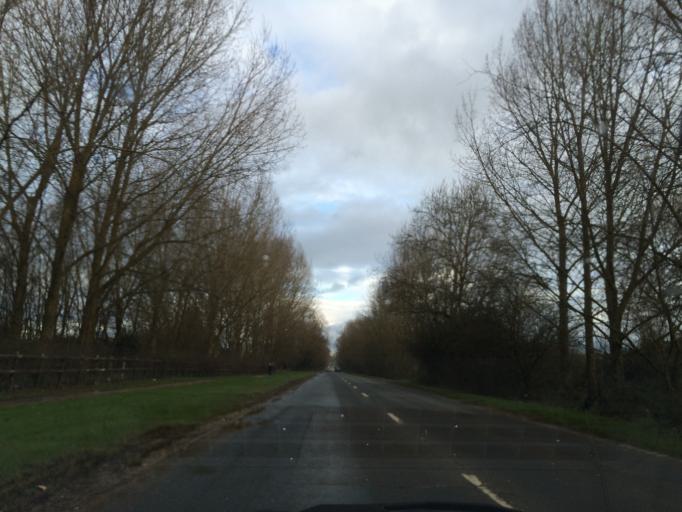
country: GB
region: England
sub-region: Wiltshire
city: Leigh
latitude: 51.6698
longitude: -1.9037
